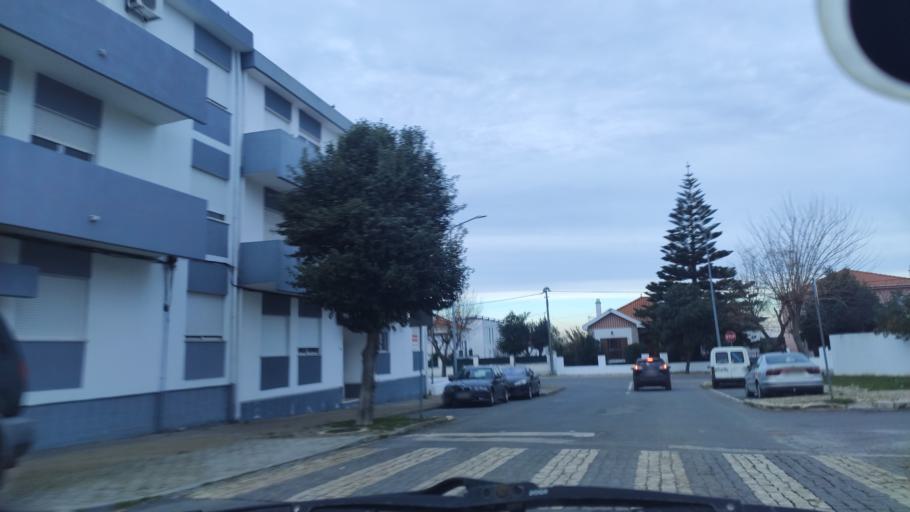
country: PT
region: Beja
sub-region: Beja
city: Ferreira do Alentejo
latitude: 38.0585
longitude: -8.1114
